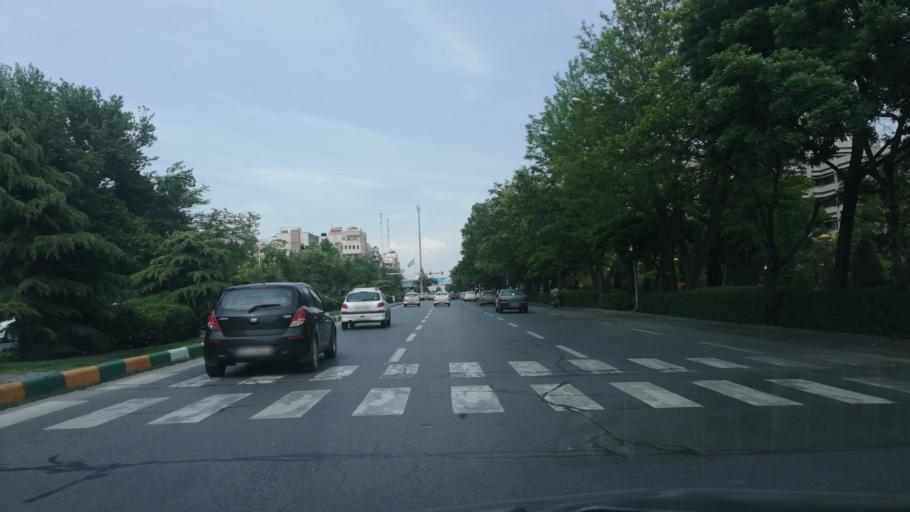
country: IR
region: Razavi Khorasan
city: Mashhad
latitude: 36.3183
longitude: 59.5640
